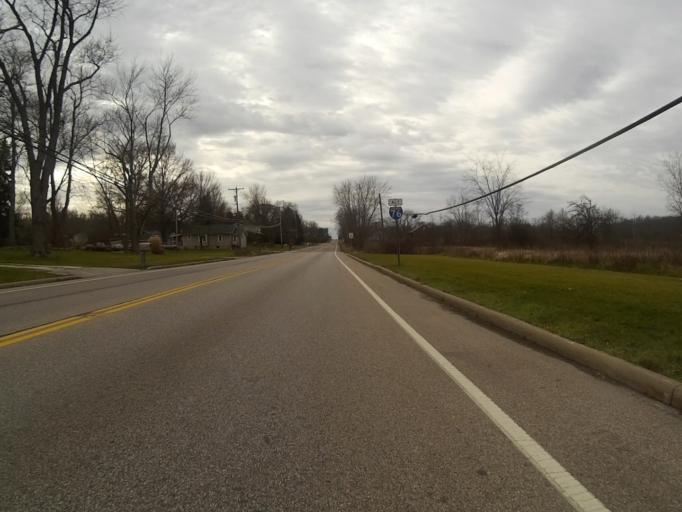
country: US
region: Ohio
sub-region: Portage County
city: Brimfield
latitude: 41.0968
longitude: -81.3463
